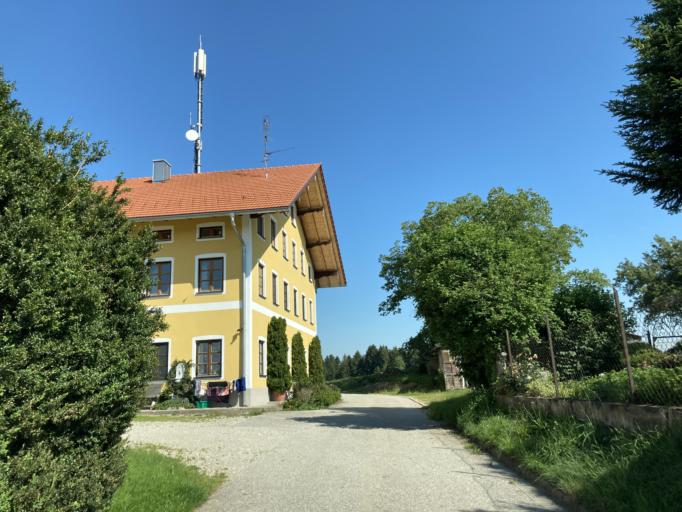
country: DE
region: Bavaria
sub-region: Upper Bavaria
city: Hoslwang
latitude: 47.9595
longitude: 12.3225
